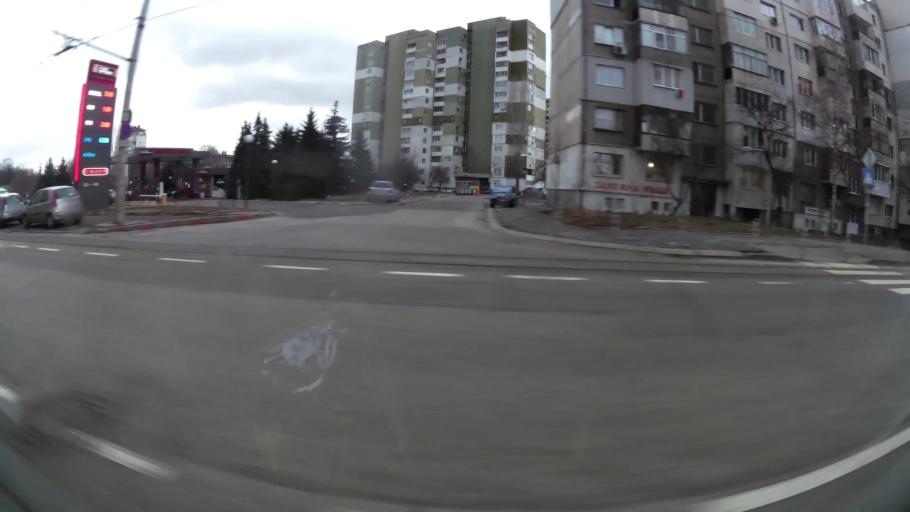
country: BG
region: Sofia-Capital
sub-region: Stolichna Obshtina
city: Sofia
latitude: 42.7373
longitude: 23.2960
